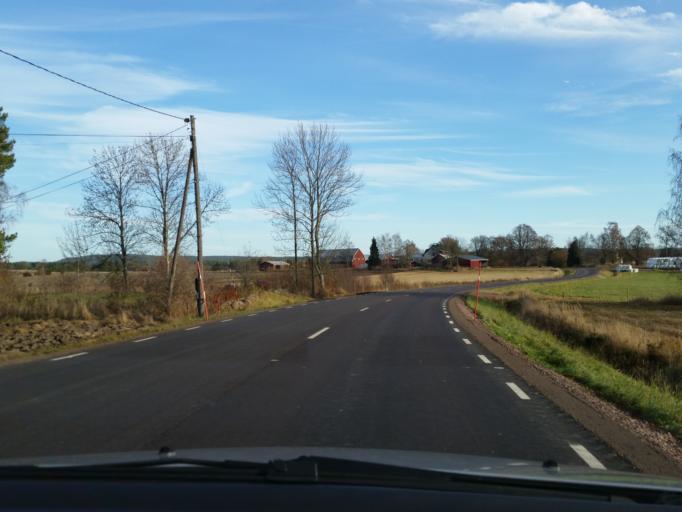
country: AX
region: Alands landsbygd
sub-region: Saltvik
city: Saltvik
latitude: 60.3182
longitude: 19.9911
